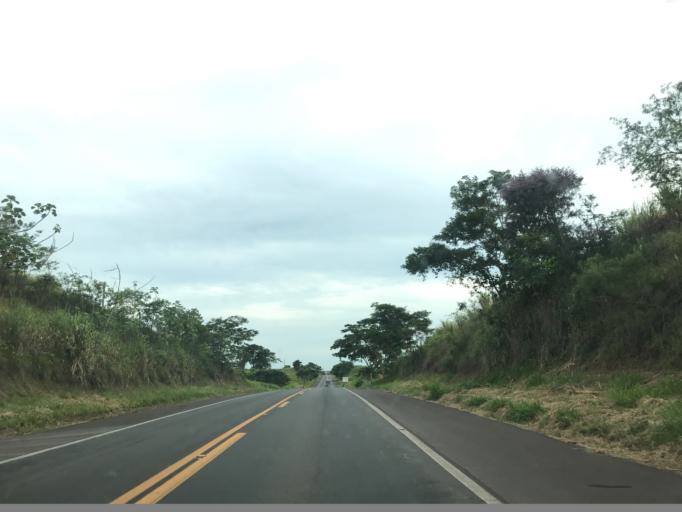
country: BR
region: Sao Paulo
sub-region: Birigui
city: Birigui
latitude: -21.5931
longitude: -50.4623
